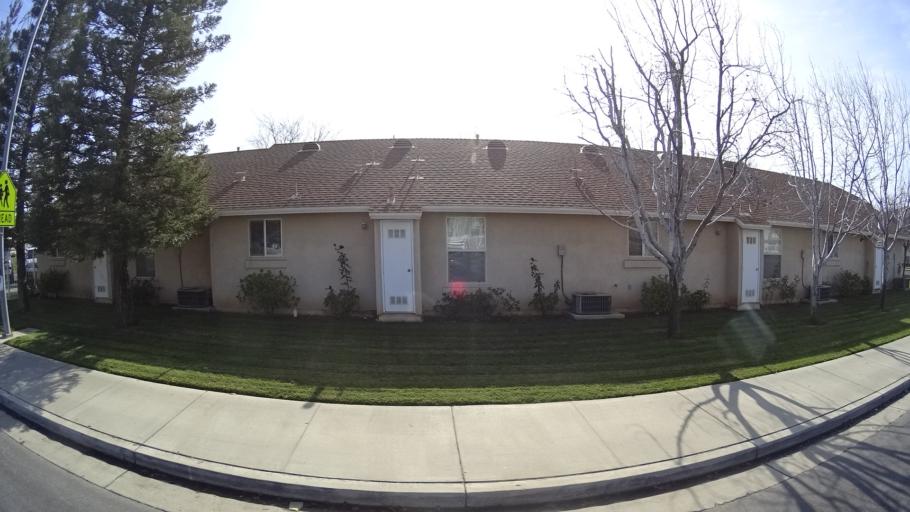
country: US
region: California
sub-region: Kern County
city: Bakersfield
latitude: 35.3981
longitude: -118.9209
